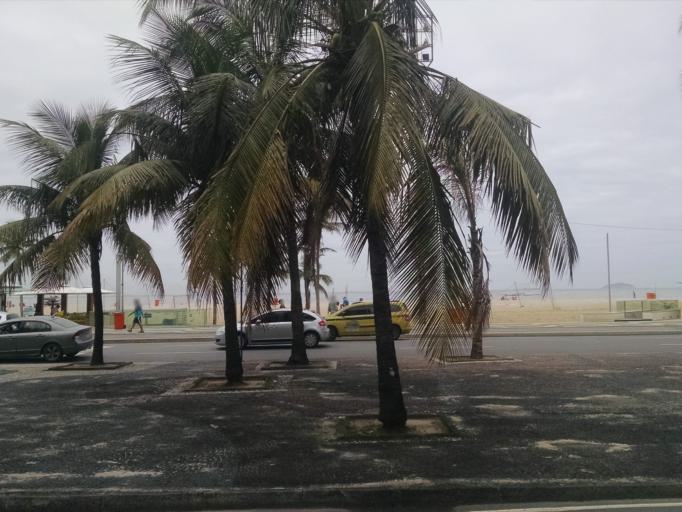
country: BR
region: Rio de Janeiro
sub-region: Rio De Janeiro
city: Rio de Janeiro
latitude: -22.9715
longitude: -43.1843
